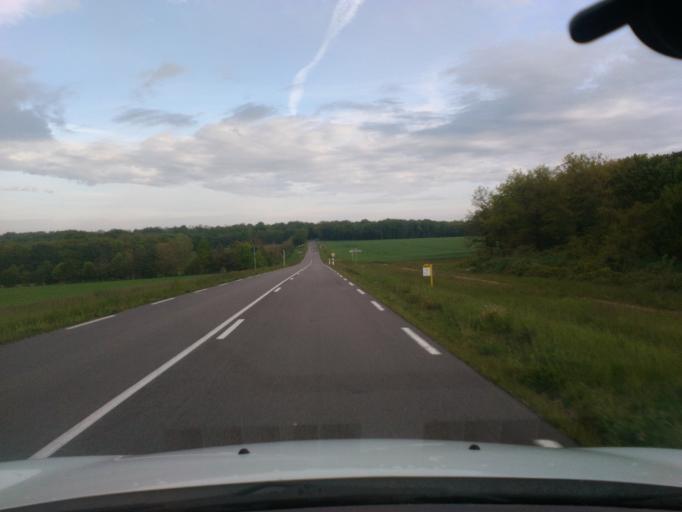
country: FR
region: Champagne-Ardenne
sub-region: Departement de la Haute-Marne
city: Lavilleneuve-au-Roi
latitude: 48.2019
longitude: 4.9400
